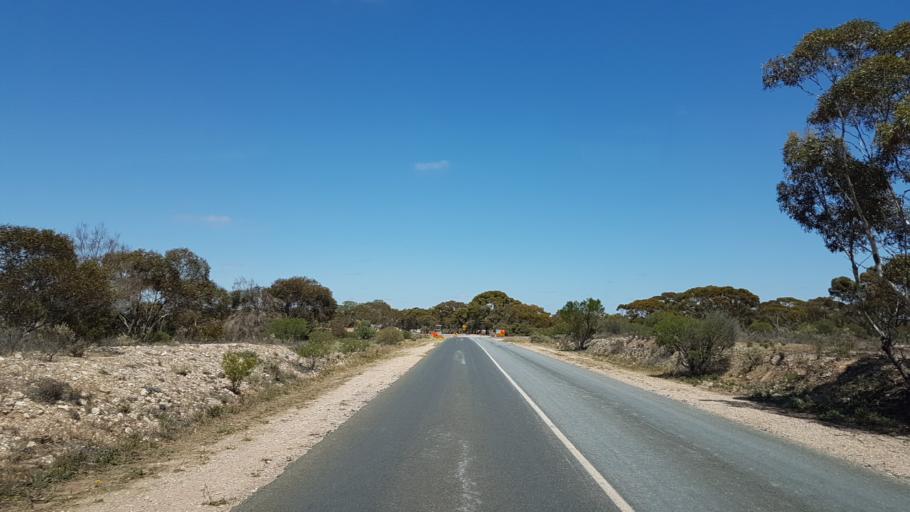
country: AU
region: South Australia
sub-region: Loxton Waikerie
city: Waikerie
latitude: -34.1863
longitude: 140.0194
